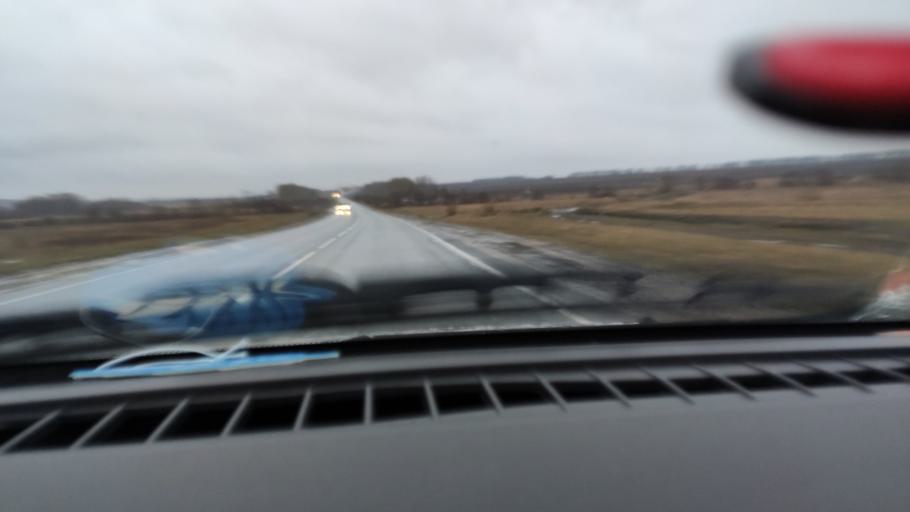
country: RU
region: Tatarstan
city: Mendeleyevsk
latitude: 55.9691
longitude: 52.3174
